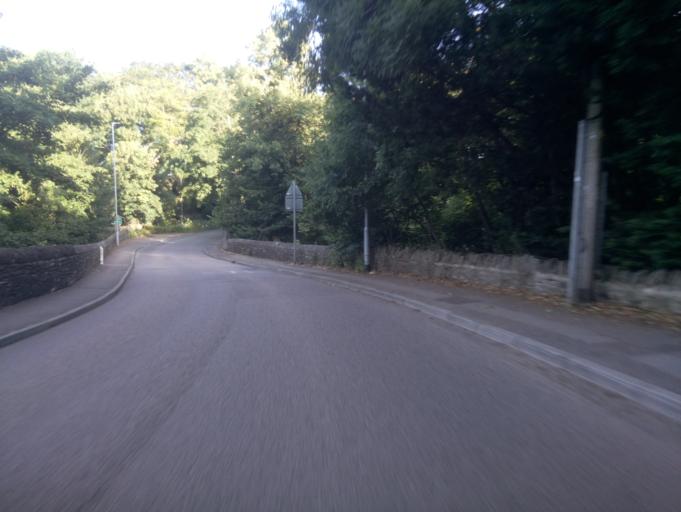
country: GB
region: England
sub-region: South Gloucestershire
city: Mangotsfield
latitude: 51.4971
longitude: -2.5135
